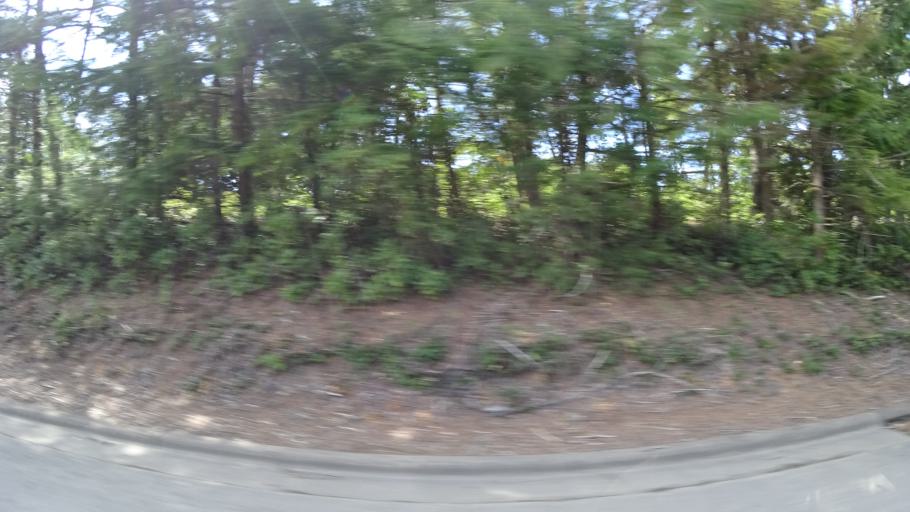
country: US
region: Oregon
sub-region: Lincoln County
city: Lincoln Beach
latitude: 44.8642
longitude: -124.0366
